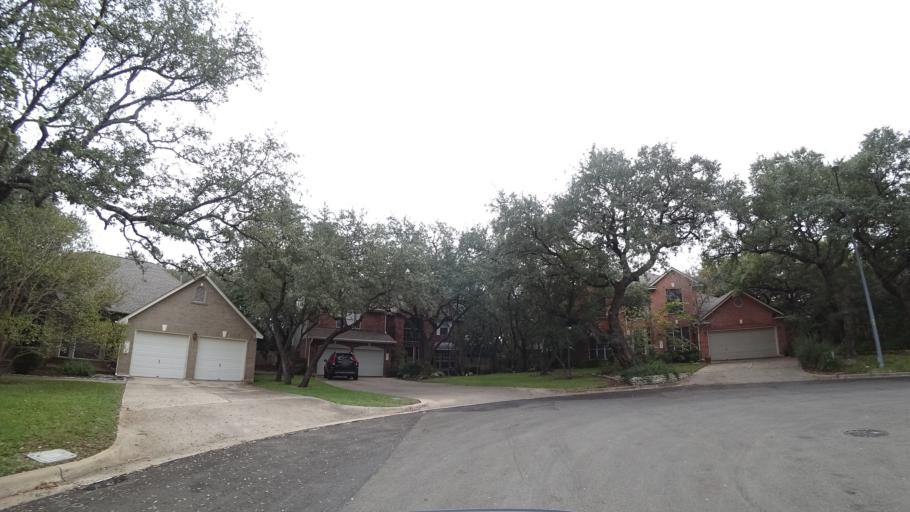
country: US
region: Texas
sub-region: Travis County
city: Shady Hollow
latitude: 30.2166
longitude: -97.8783
